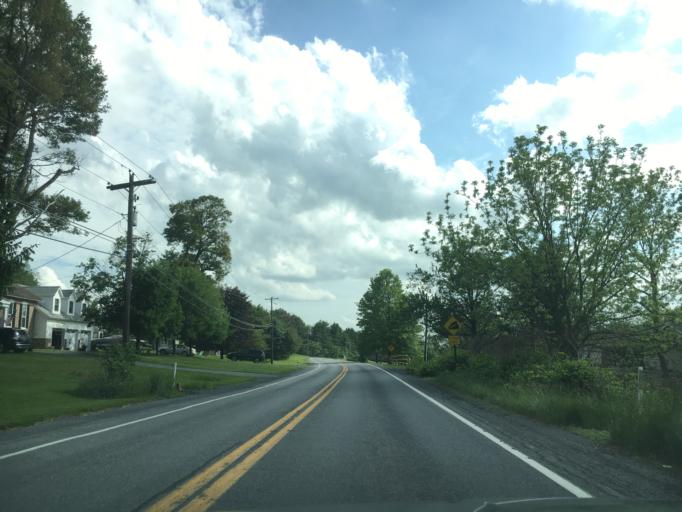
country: US
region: Pennsylvania
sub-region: Northampton County
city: Cherryville
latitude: 40.7508
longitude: -75.5407
